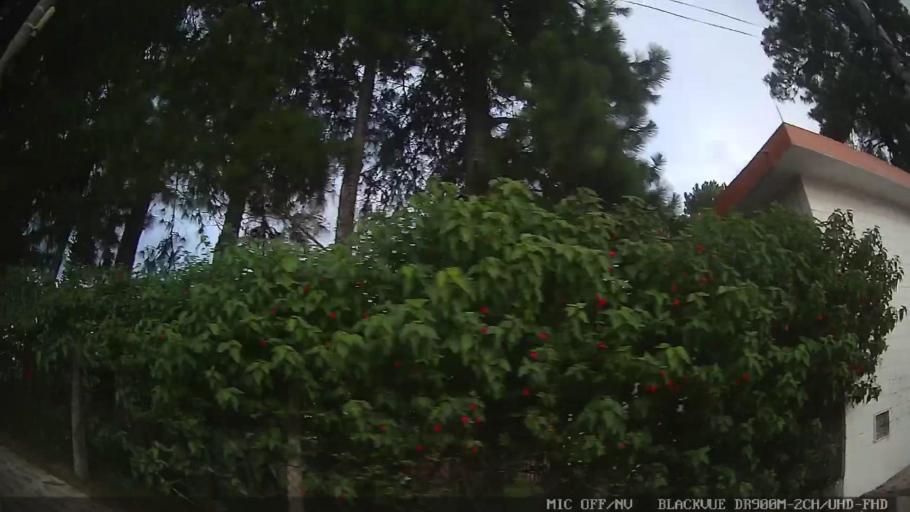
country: BR
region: Sao Paulo
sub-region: Suzano
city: Suzano
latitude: -23.5248
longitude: -46.3039
